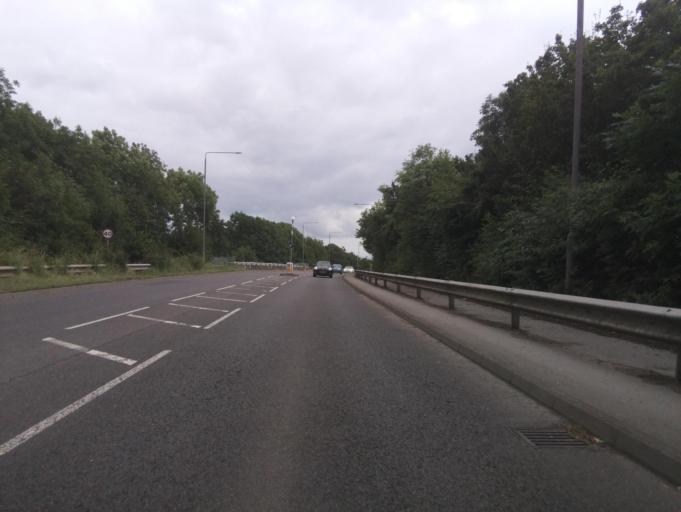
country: GB
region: England
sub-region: Nottinghamshire
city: Radcliffe on Trent
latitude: 52.9656
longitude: -1.0693
